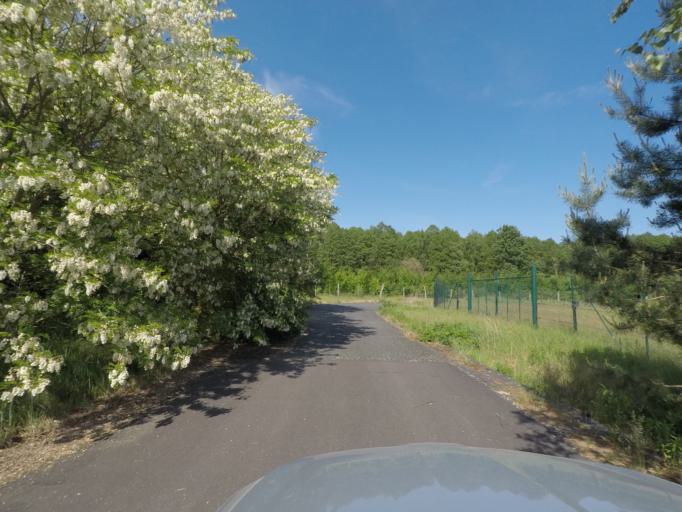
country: DE
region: Brandenburg
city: Britz
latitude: 52.8596
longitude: 13.7670
